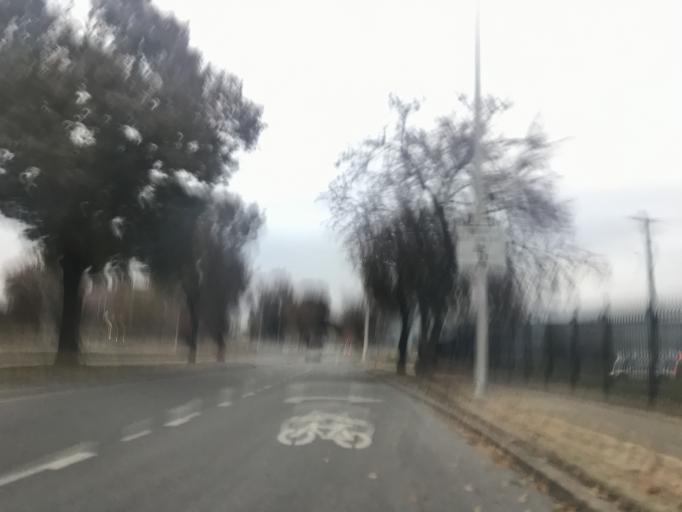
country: US
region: Kentucky
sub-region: Jefferson County
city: Louisville
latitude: 38.2497
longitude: -85.7728
